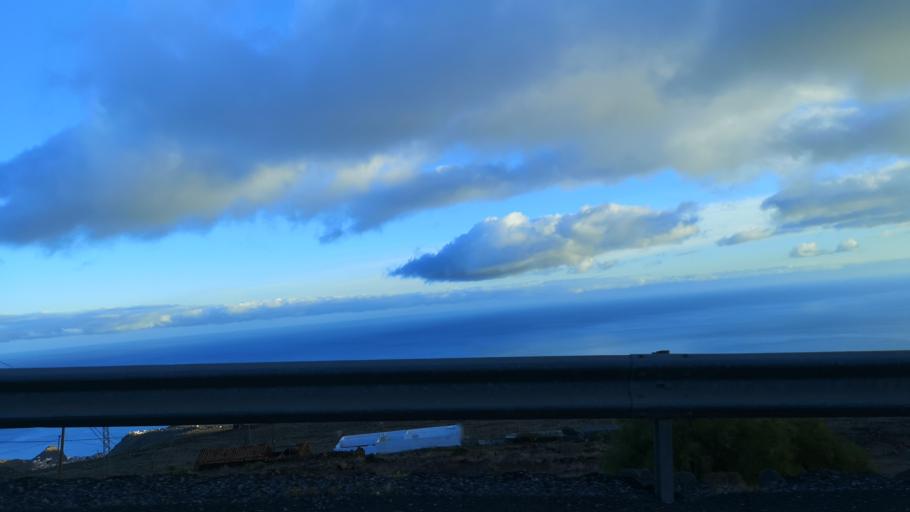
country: ES
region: Canary Islands
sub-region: Provincia de Santa Cruz de Tenerife
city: Alajero
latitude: 28.0446
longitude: -17.2277
